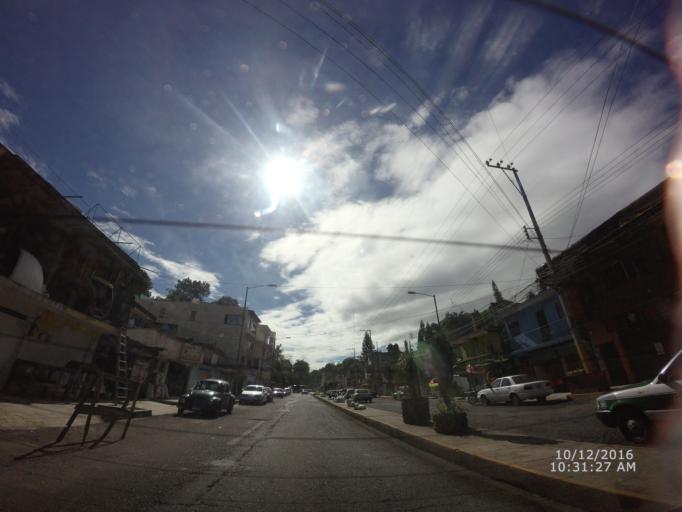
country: TR
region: Sivas
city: Karayun
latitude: 39.6711
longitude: 37.2576
